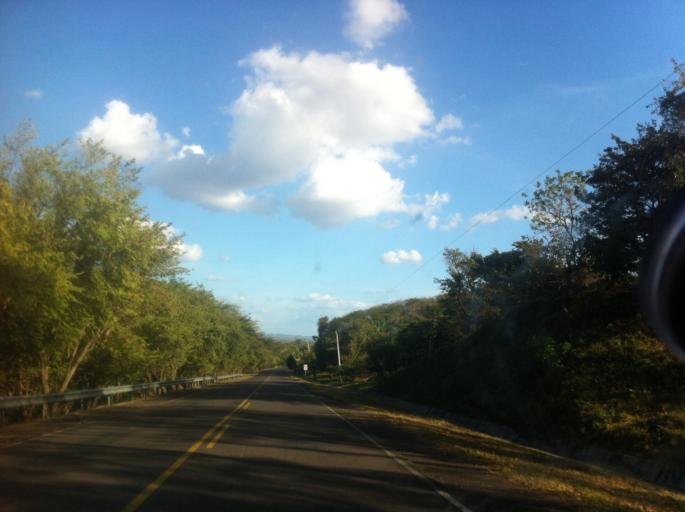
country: NI
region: Chontales
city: Acoyapa
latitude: 11.8553
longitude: -85.0570
